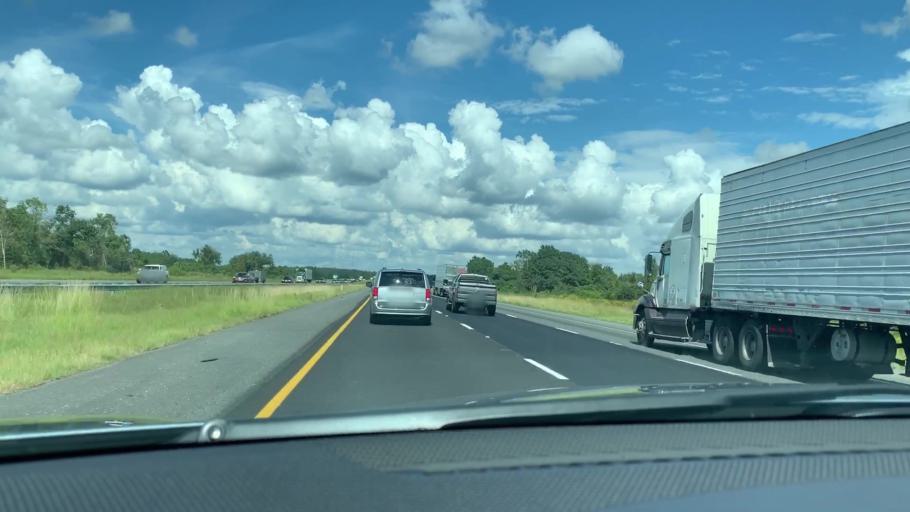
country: US
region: Georgia
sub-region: Camden County
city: Woodbine
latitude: 31.0303
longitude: -81.6550
